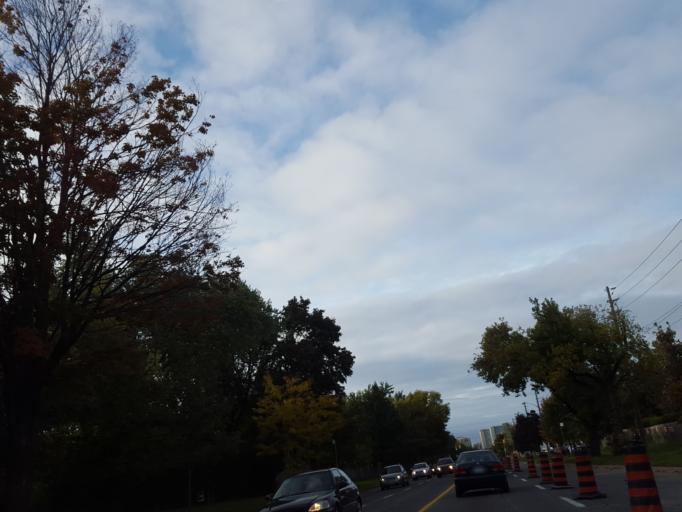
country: CA
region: Ontario
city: Scarborough
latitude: 43.7832
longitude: -79.3099
